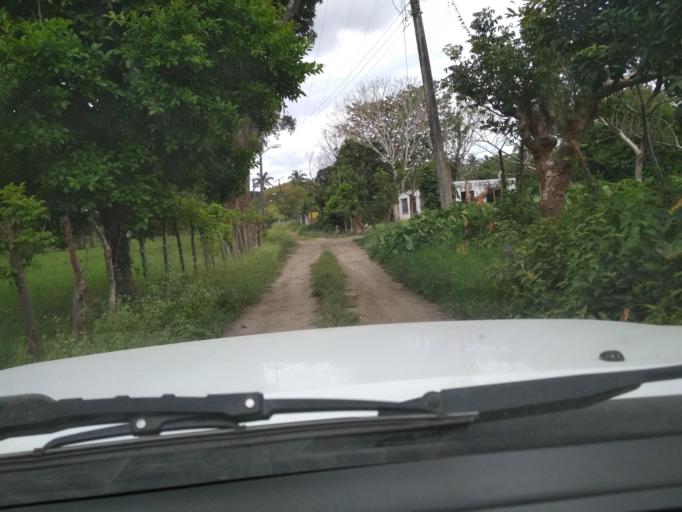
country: MX
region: Veracruz
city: El Tejar
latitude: 19.0628
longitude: -96.1552
